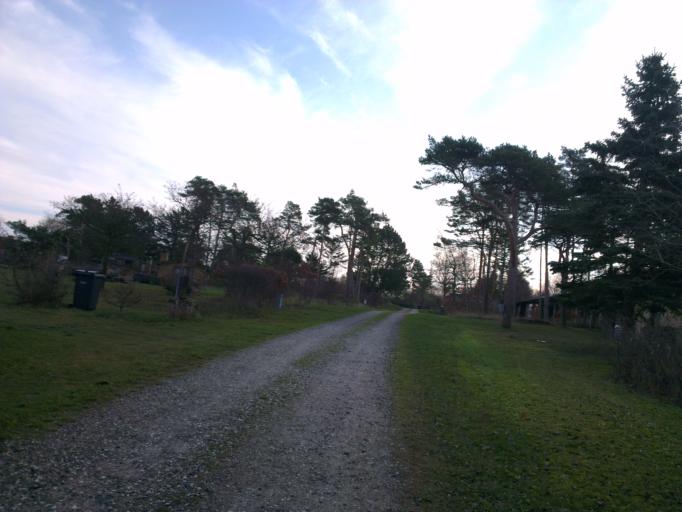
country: DK
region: Capital Region
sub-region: Frederikssund Kommune
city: Jaegerspris
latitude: 55.8416
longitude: 11.9608
